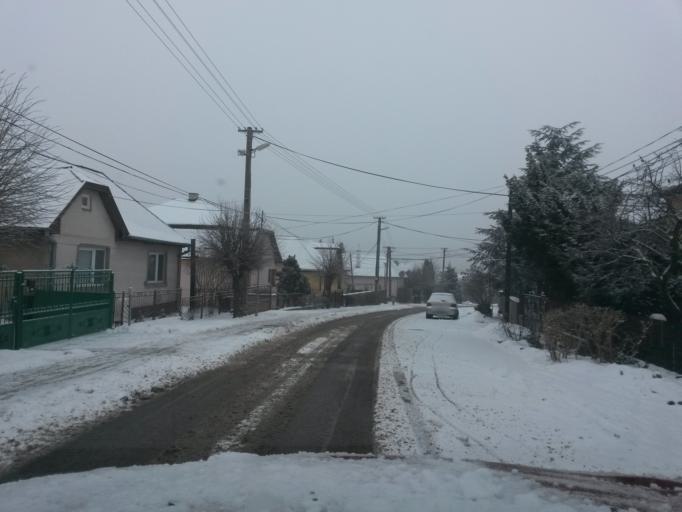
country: SK
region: Kosicky
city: Kosice
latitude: 48.7287
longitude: 21.3037
